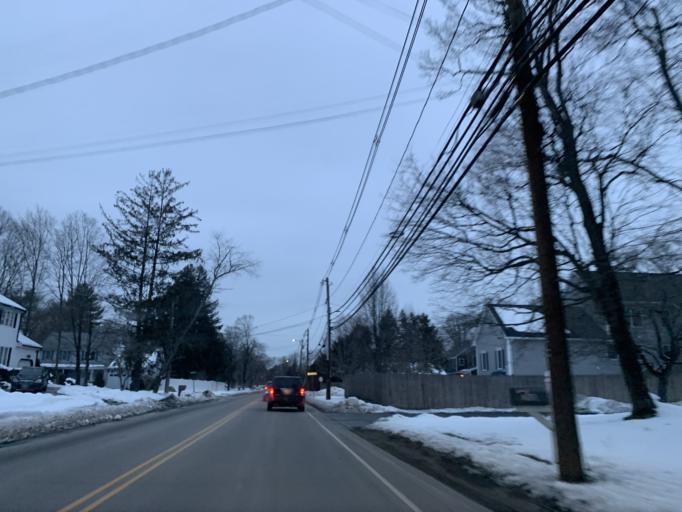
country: US
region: Massachusetts
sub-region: Norfolk County
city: Canton
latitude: 42.1488
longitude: -71.1225
